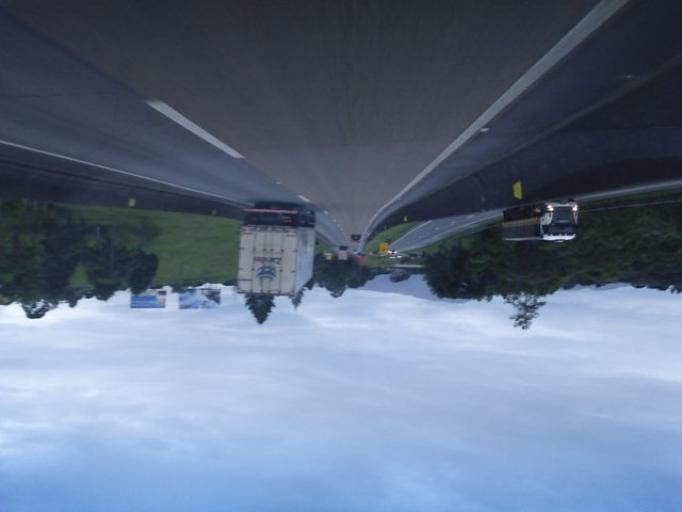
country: BR
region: Parana
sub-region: Sao Jose Dos Pinhais
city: Sao Jose dos Pinhais
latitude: -25.8435
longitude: -49.1011
